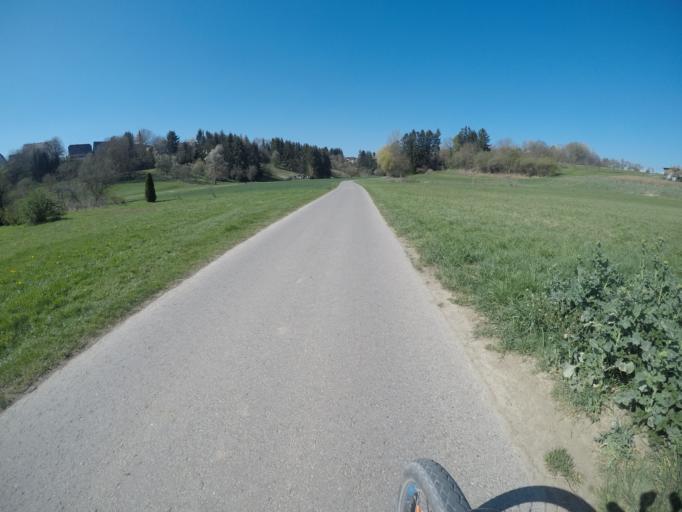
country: DE
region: Baden-Wuerttemberg
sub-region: Regierungsbezirk Stuttgart
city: Herrenberg
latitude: 48.5551
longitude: 8.8776
